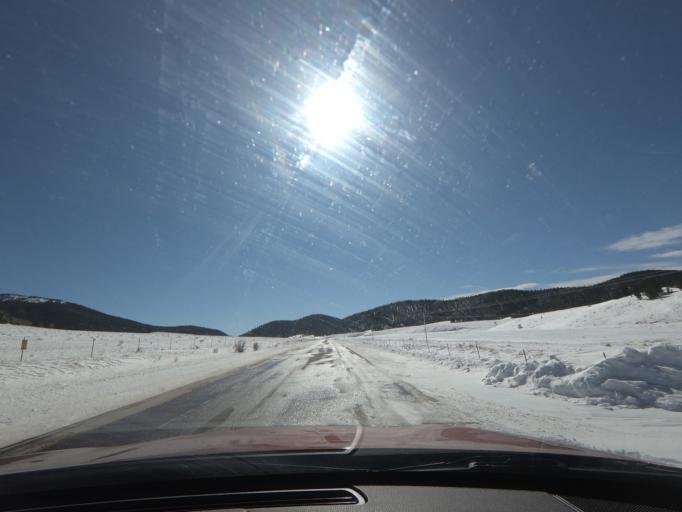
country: US
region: Colorado
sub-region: Teller County
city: Cripple Creek
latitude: 38.7691
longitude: -105.1188
